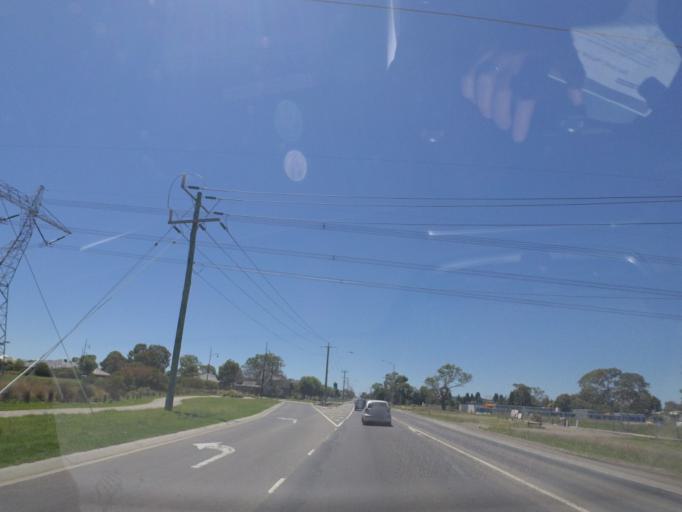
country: AU
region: Victoria
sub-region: Whittlesea
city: Epping
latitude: -37.6342
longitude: 145.0269
